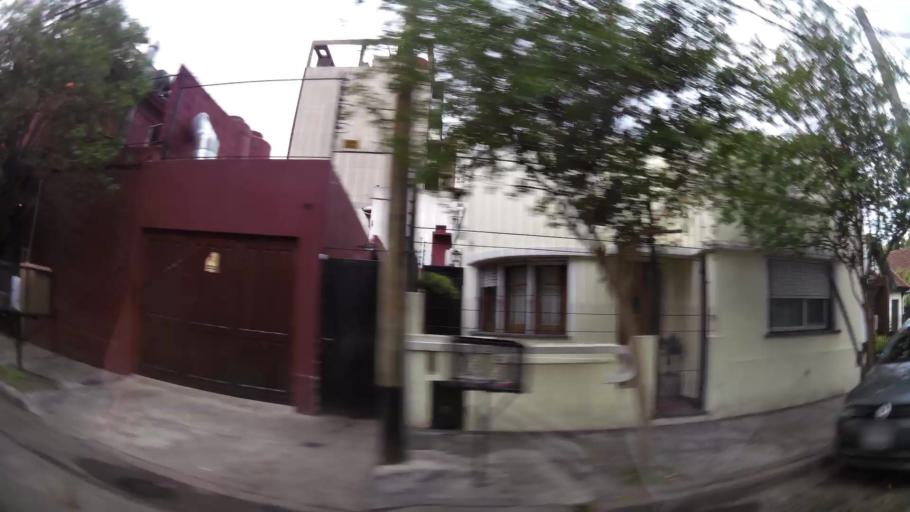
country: AR
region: Buenos Aires
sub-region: Partido de Quilmes
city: Quilmes
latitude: -34.7262
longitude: -58.2543
